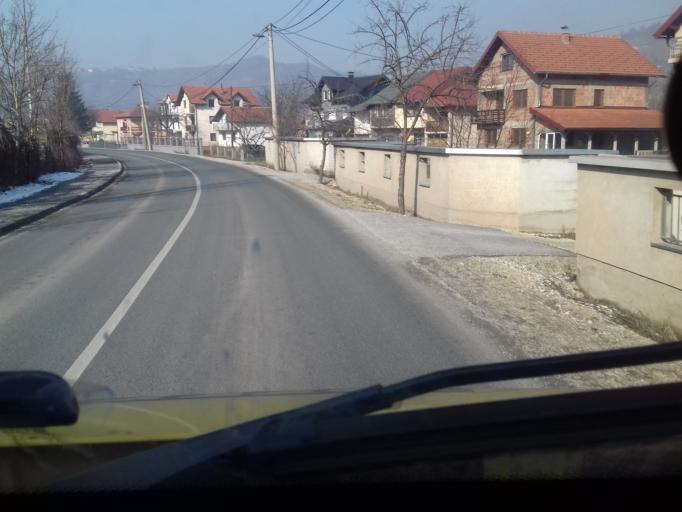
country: BA
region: Federation of Bosnia and Herzegovina
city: Ilijas
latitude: 43.9354
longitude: 18.2985
